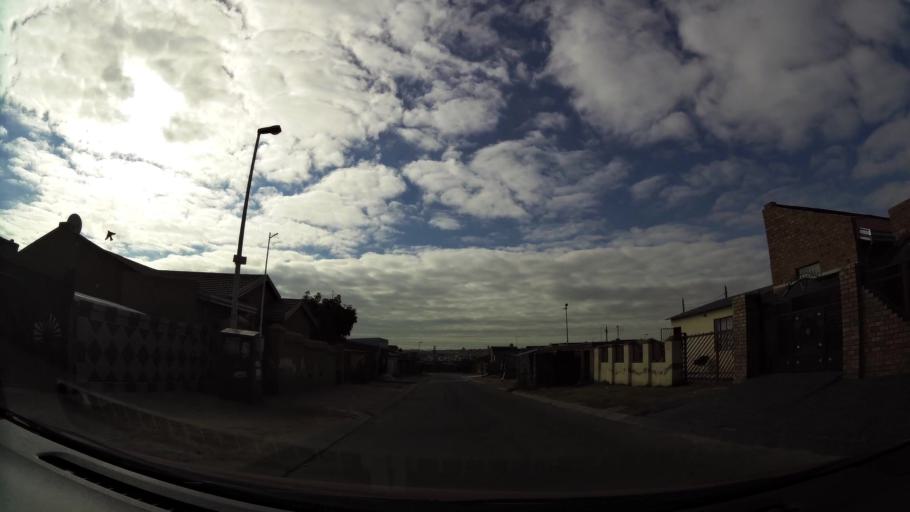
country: ZA
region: Gauteng
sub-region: City of Johannesburg Metropolitan Municipality
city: Modderfontein
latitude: -26.0415
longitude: 28.1841
